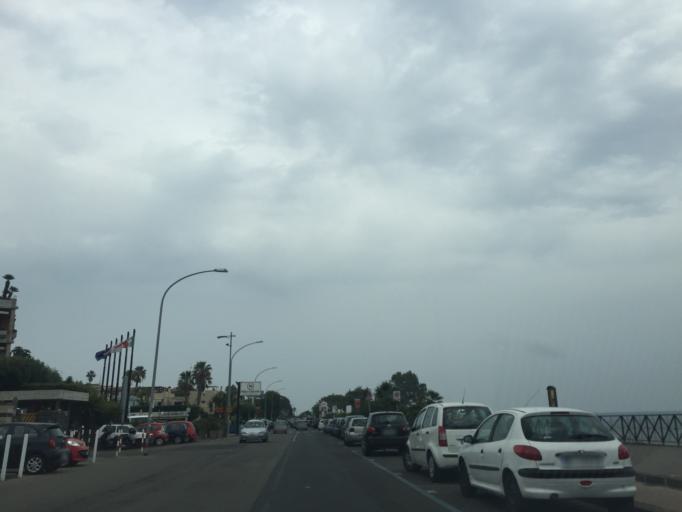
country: IT
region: Sicily
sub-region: Catania
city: Aci Castello
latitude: 37.5417
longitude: 15.1360
